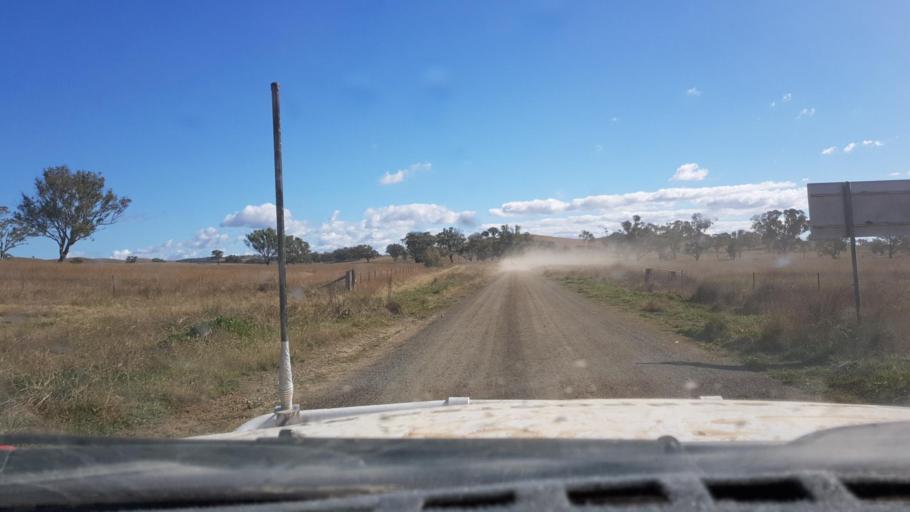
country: AU
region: New South Wales
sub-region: Narrabri
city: Blair Athol
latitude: -30.5048
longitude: 150.4417
